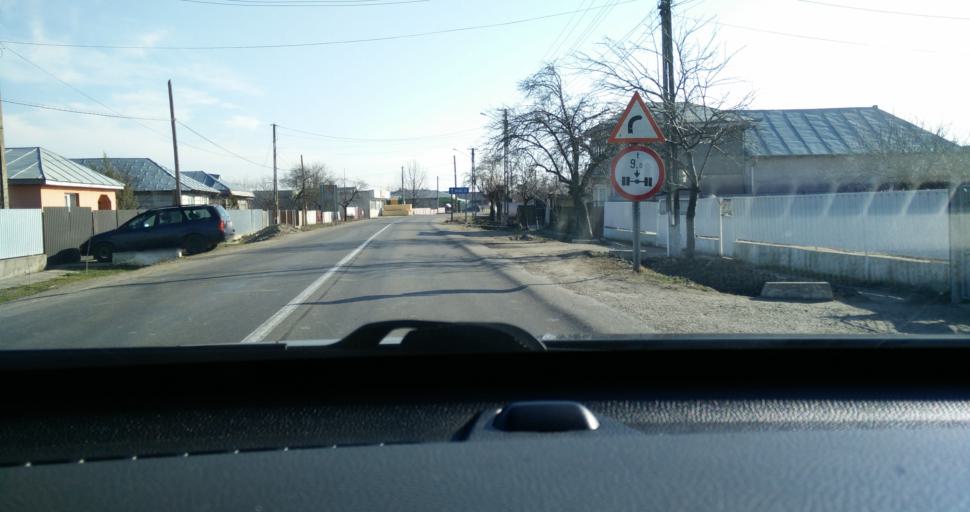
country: RO
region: Vrancea
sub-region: Comuna Nanesti
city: Nanesti
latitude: 45.5514
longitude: 27.5005
